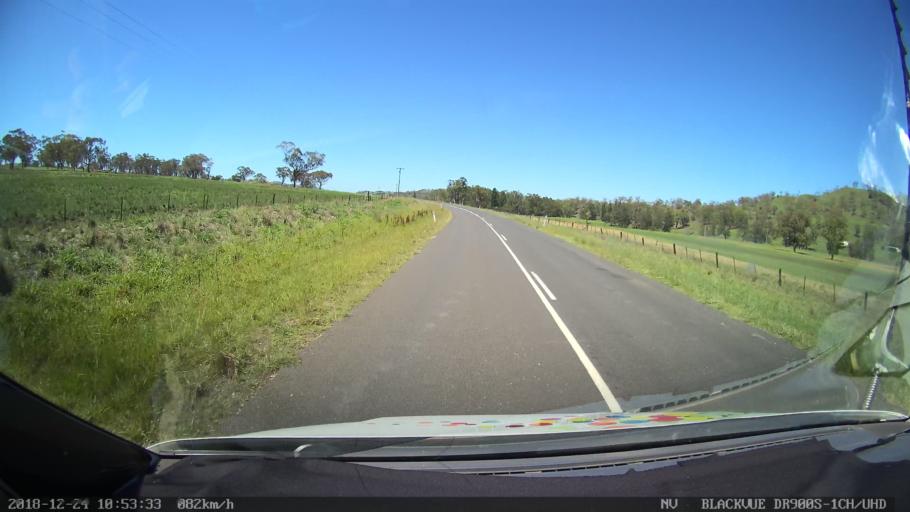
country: AU
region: New South Wales
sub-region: Upper Hunter Shire
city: Merriwa
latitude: -31.9929
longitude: 150.4202
